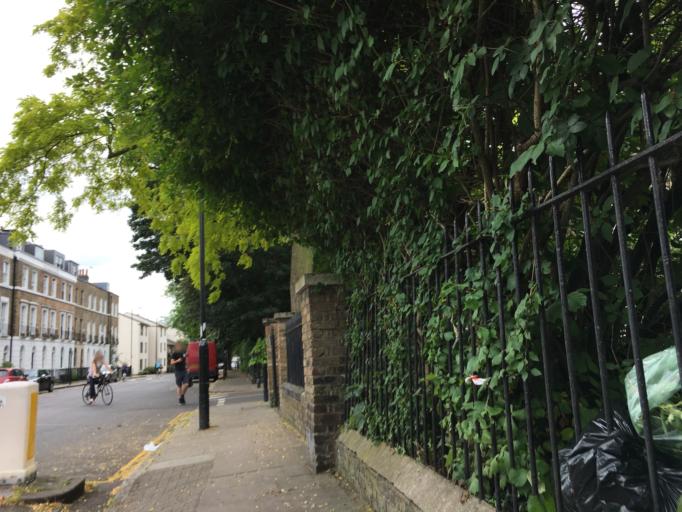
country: GB
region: England
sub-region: Greater London
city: Barnsbury
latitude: 51.5424
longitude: -0.1102
